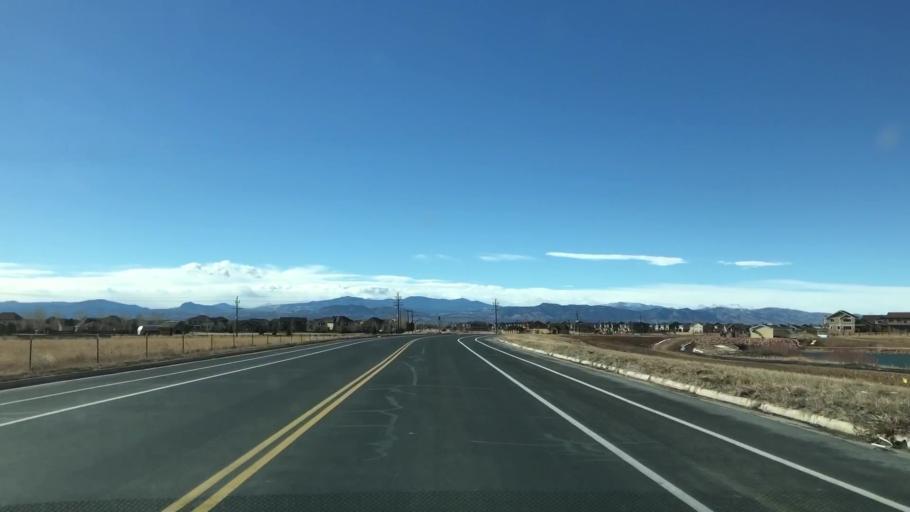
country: US
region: Colorado
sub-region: Weld County
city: Windsor
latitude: 40.5083
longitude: -104.9463
